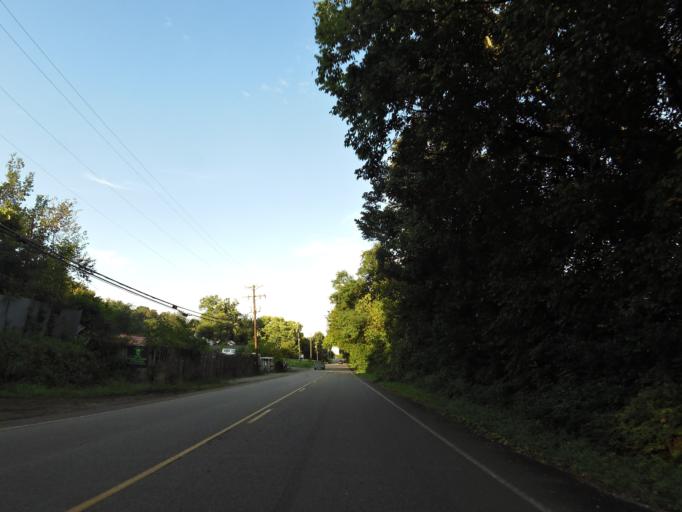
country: US
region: Tennessee
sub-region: Knox County
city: Mascot
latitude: 36.0320
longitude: -83.8287
